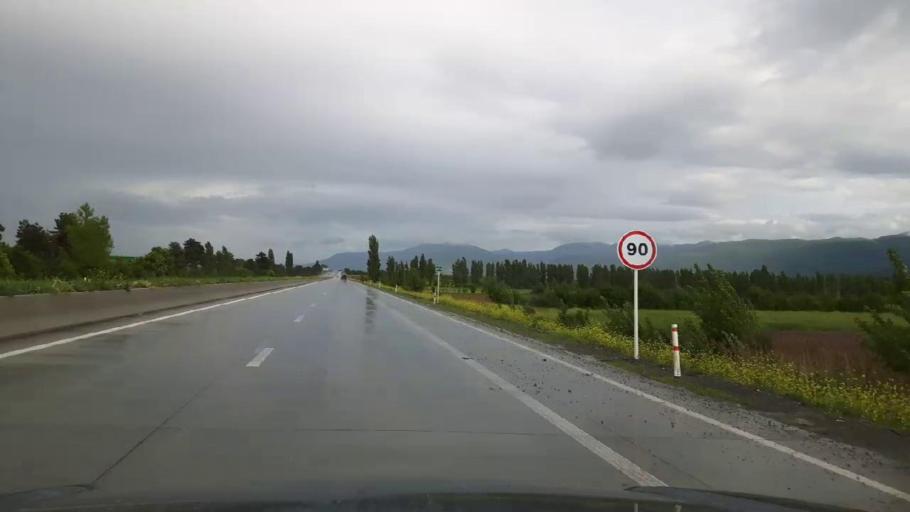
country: GE
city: Agara
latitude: 42.0456
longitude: 43.9196
